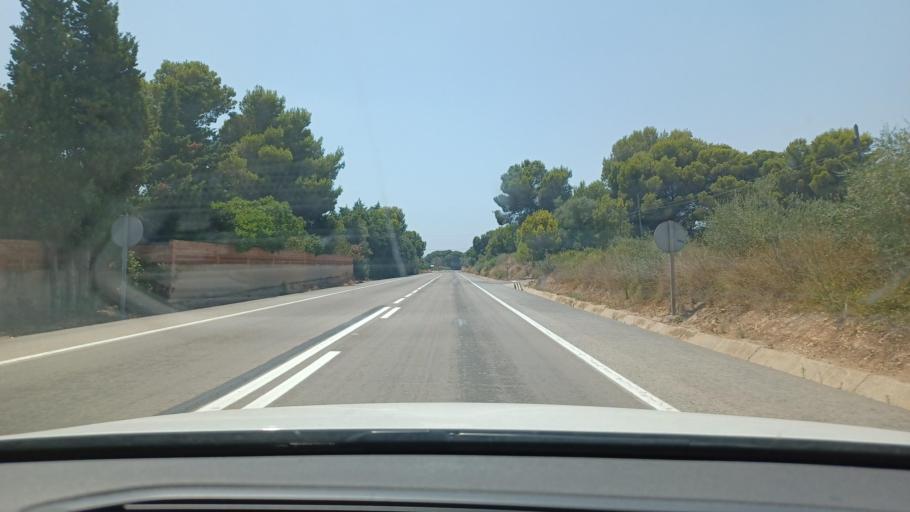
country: ES
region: Catalonia
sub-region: Provincia de Tarragona
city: Alcanar
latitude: 40.5666
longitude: 0.5367
